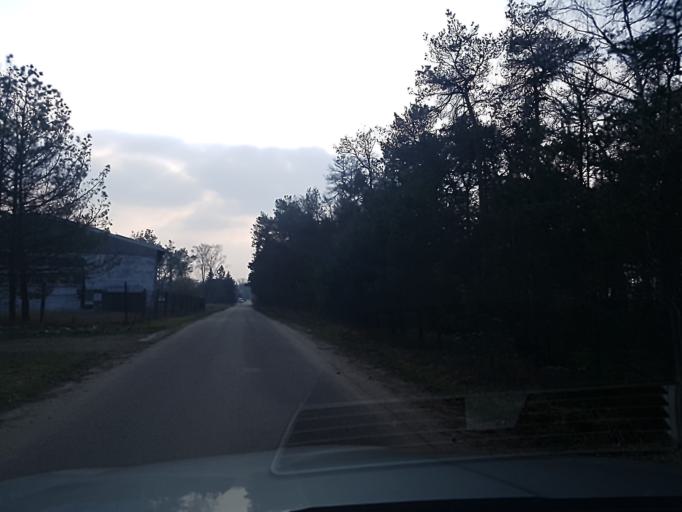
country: DE
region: Brandenburg
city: Doberlug-Kirchhain
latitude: 51.6140
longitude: 13.6025
